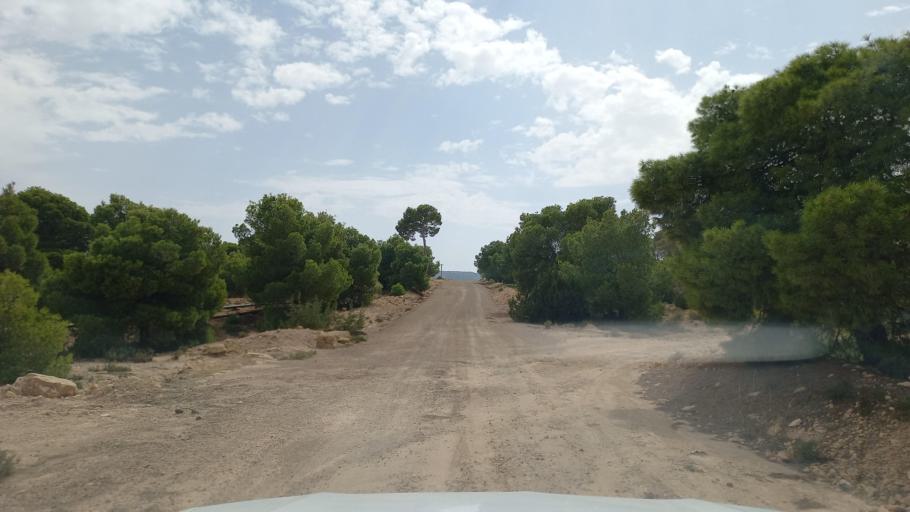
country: TN
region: Al Qasrayn
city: Kasserine
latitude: 35.3804
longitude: 8.8802
